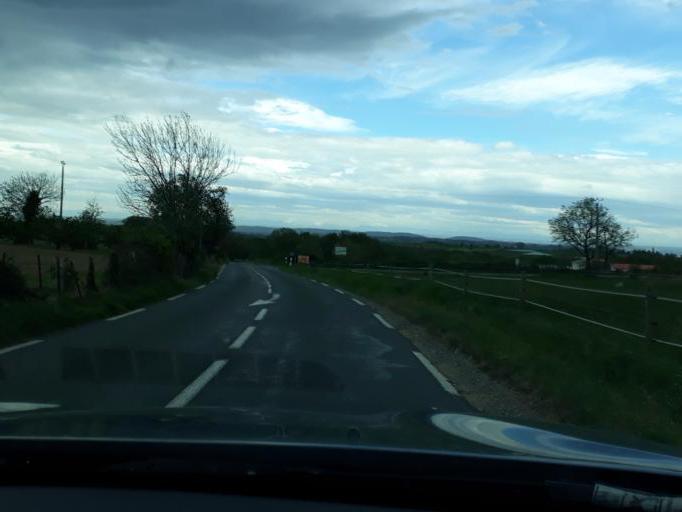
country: FR
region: Rhone-Alpes
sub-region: Departement du Rhone
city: Soucieu-en-Jarrest
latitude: 45.6781
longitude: 4.7188
